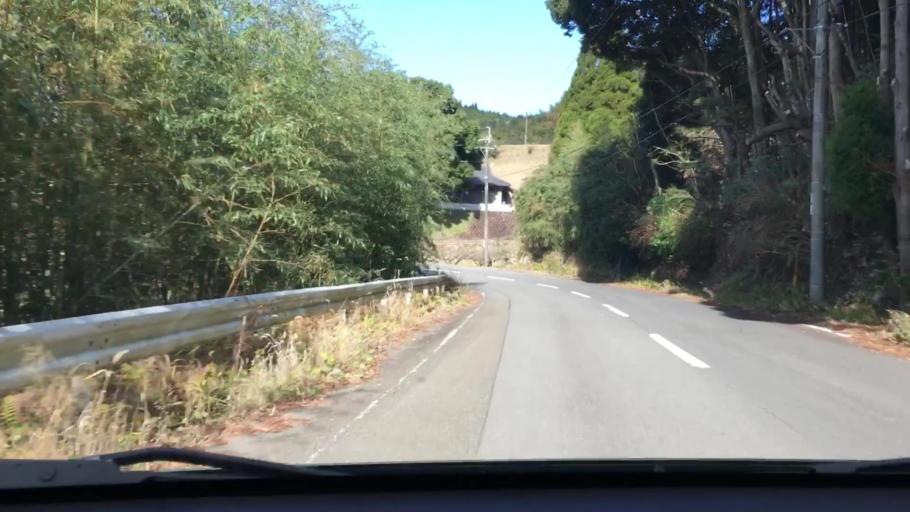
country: JP
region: Kagoshima
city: Ijuin
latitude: 31.7303
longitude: 130.4194
